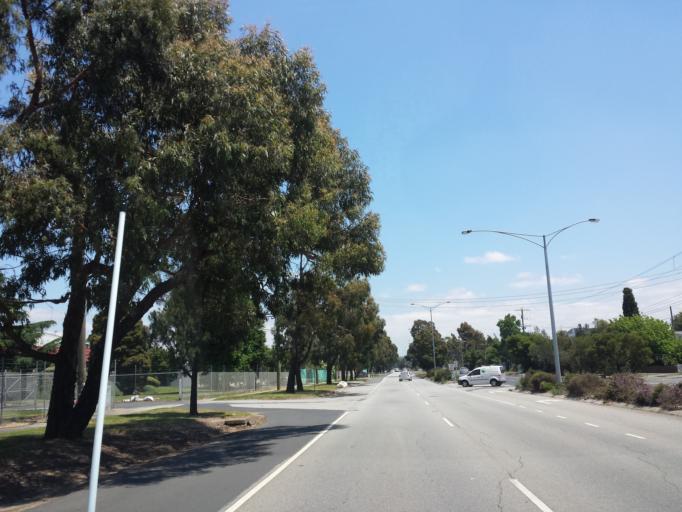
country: AU
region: Victoria
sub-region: Maroondah
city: Bayswater North
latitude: -37.8378
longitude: 145.2842
